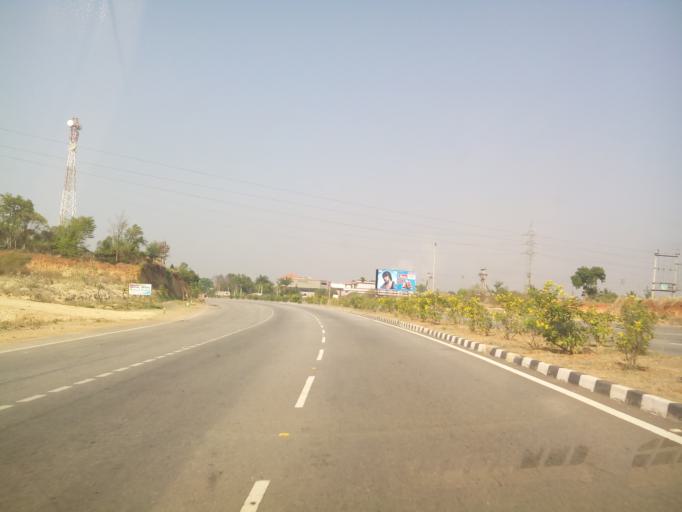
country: IN
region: Karnataka
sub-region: Tumkur
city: Kunigal
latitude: 13.0349
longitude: 77.0877
